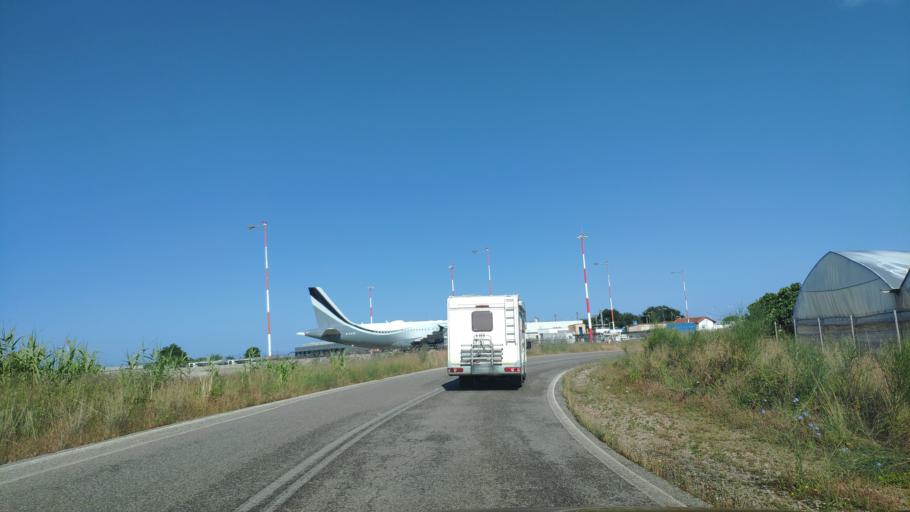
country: GR
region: Epirus
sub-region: Nomos Prevezis
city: Preveza
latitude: 38.9304
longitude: 20.7752
